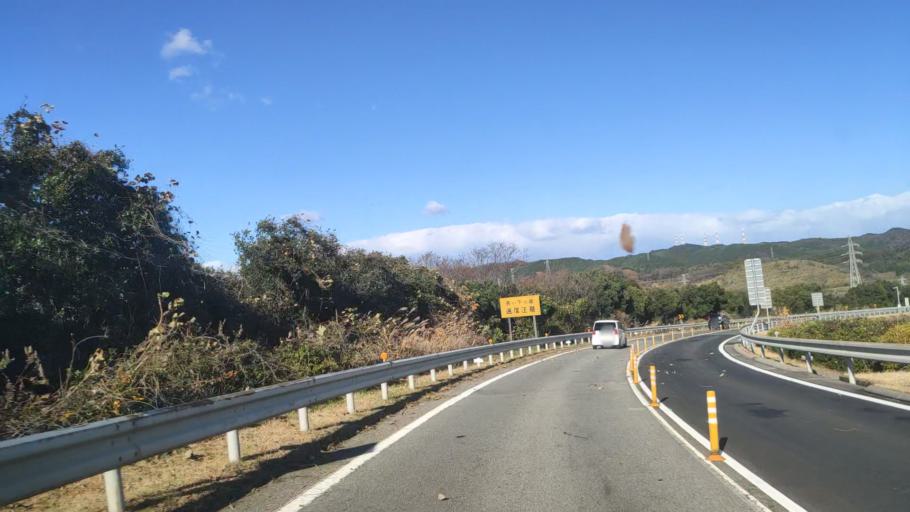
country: JP
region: Ehime
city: Saijo
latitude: 33.9155
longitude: 133.2369
